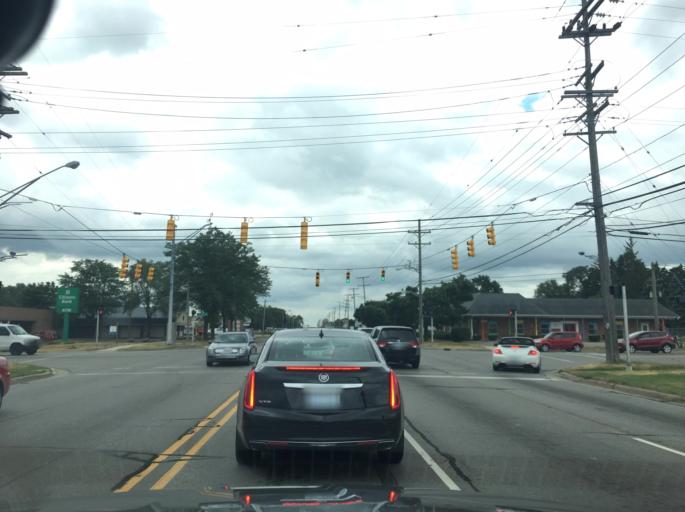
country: US
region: Michigan
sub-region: Macomb County
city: Shelby
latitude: 42.6555
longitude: -83.0334
